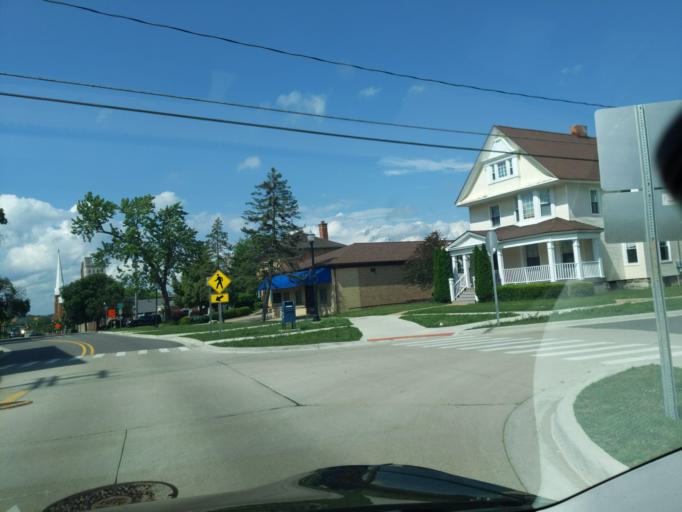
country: US
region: Michigan
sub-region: Jackson County
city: Jackson
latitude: 42.2430
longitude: -84.4088
